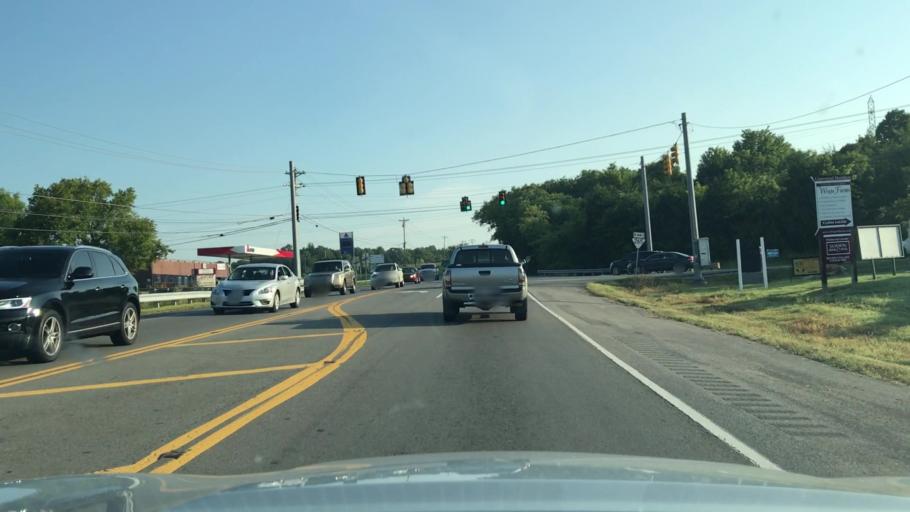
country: US
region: Tennessee
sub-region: Wilson County
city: Mount Juliet
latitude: 36.1532
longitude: -86.5162
